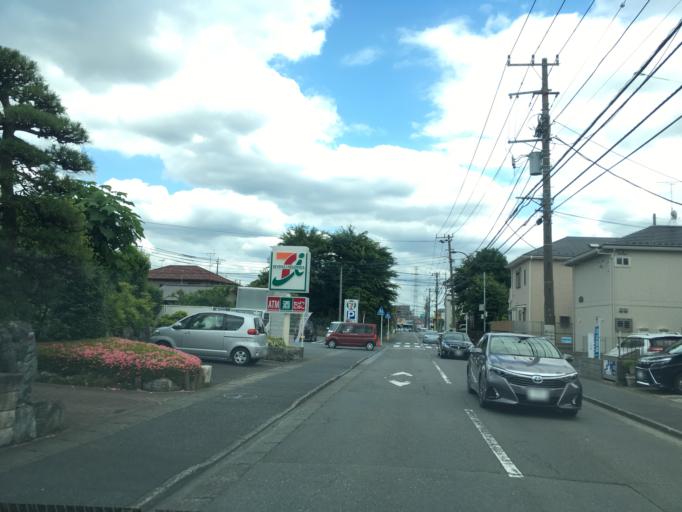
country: JP
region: Tokyo
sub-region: Machida-shi
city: Machida
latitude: 35.5633
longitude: 139.4028
